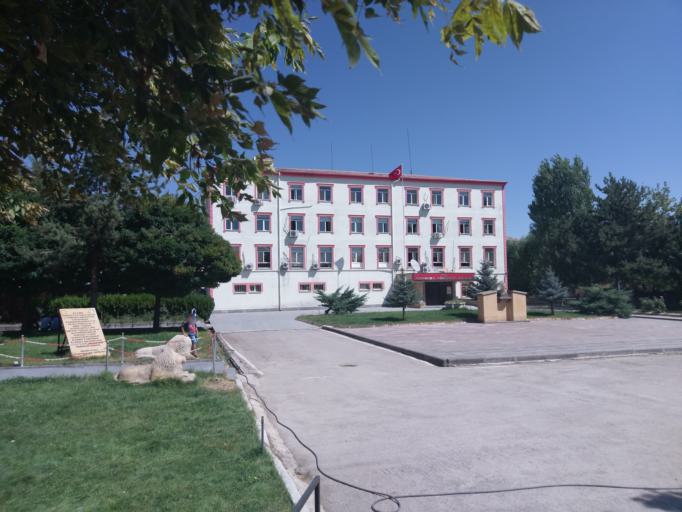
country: TR
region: Kayseri
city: Tomarza
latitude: 38.4471
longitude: 35.7986
